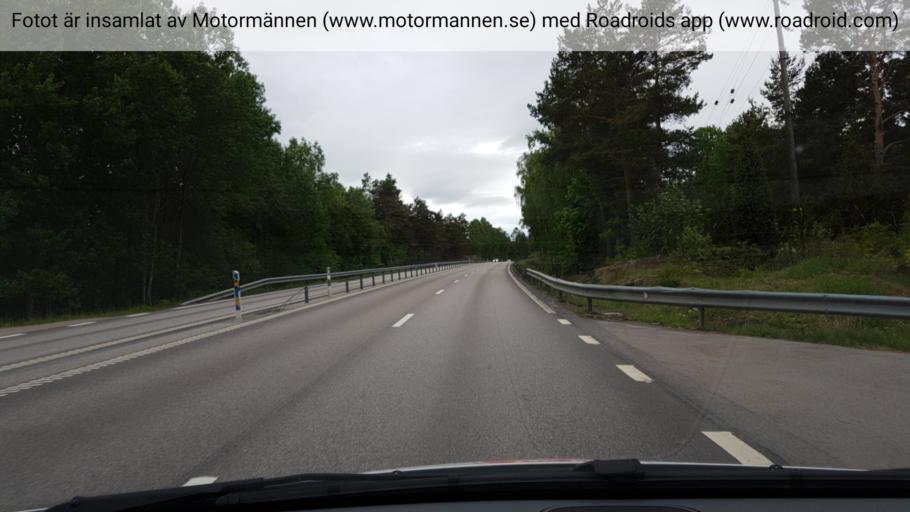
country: SE
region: Kalmar
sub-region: Oskarshamns Kommun
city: Oskarshamn
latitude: 57.3267
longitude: 16.4757
